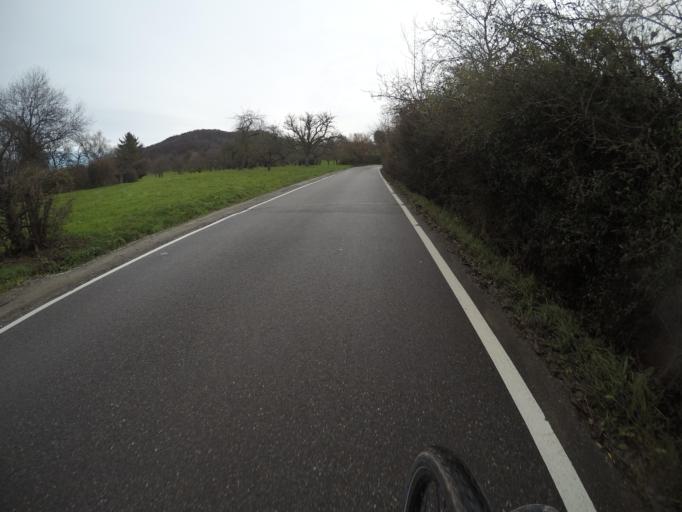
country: DE
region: Baden-Wuerttemberg
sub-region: Regierungsbezirk Stuttgart
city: Korb
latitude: 48.8577
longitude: 9.3526
